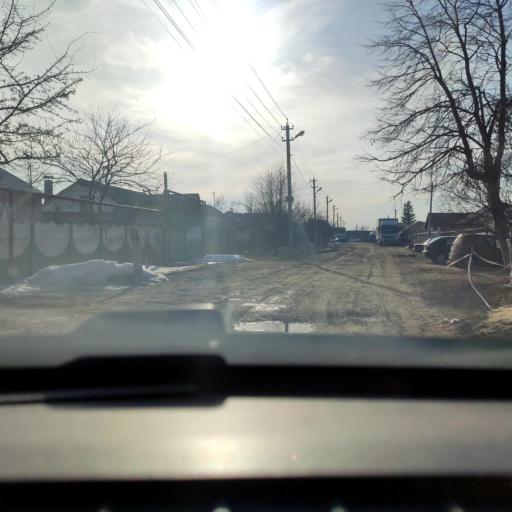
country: RU
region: Voronezj
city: Podgornoye
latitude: 51.7413
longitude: 39.1527
